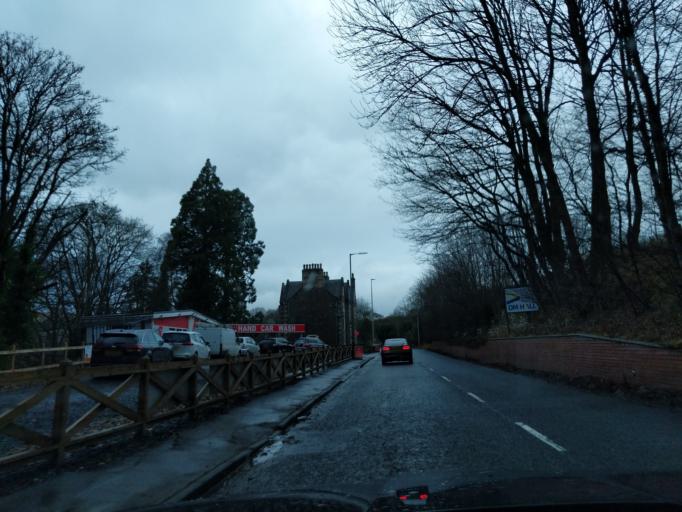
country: GB
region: Scotland
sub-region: The Scottish Borders
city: Galashiels
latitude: 55.6276
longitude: -2.8268
